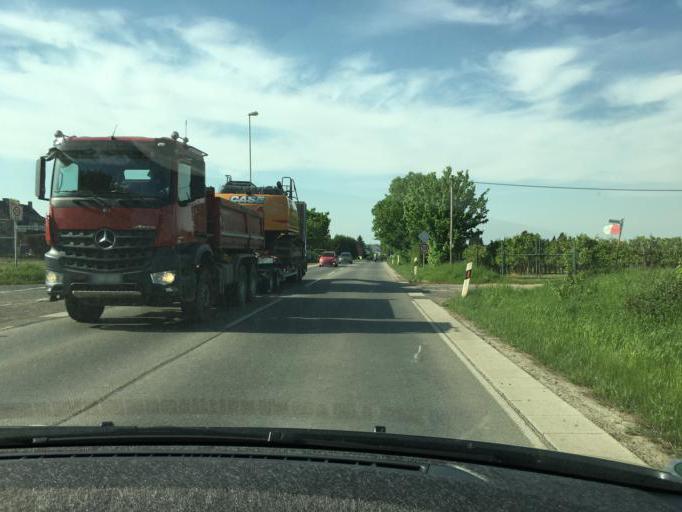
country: DE
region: North Rhine-Westphalia
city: Bruhl
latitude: 50.7909
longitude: 6.9206
